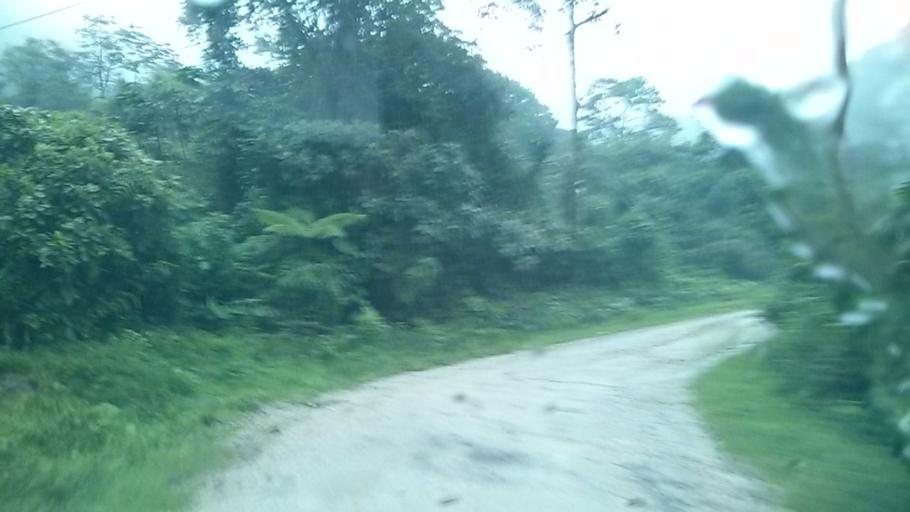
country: CR
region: San Jose
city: Ipis
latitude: 10.0216
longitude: -83.9434
